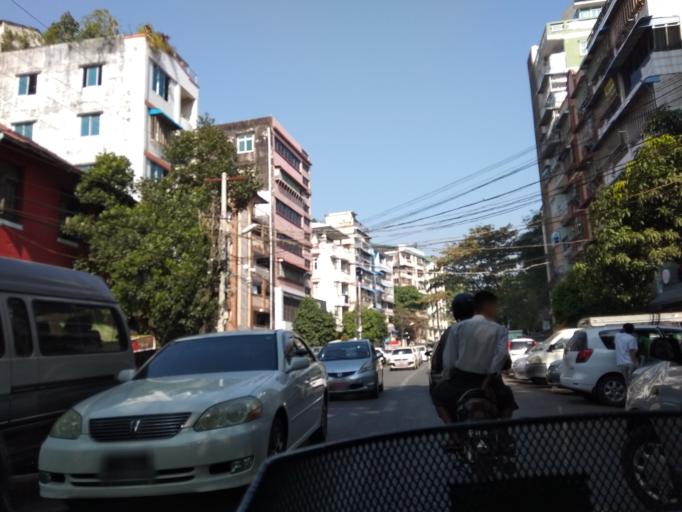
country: MM
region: Yangon
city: Yangon
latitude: 16.8043
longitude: 96.1334
